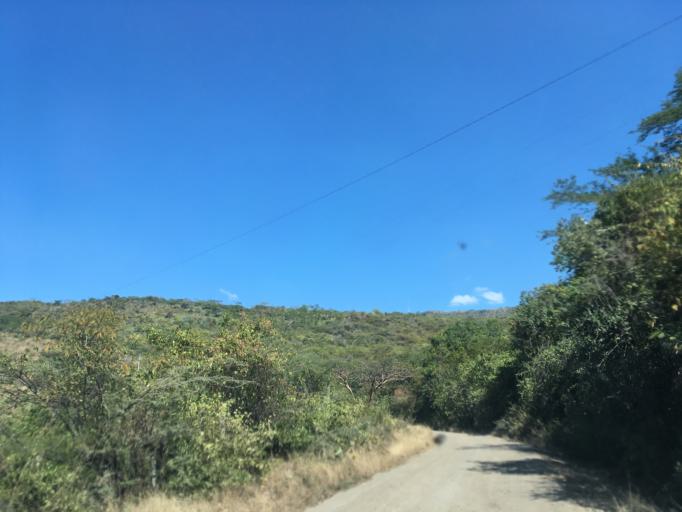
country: CO
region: Santander
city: Barichara
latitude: 6.6360
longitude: -73.2468
